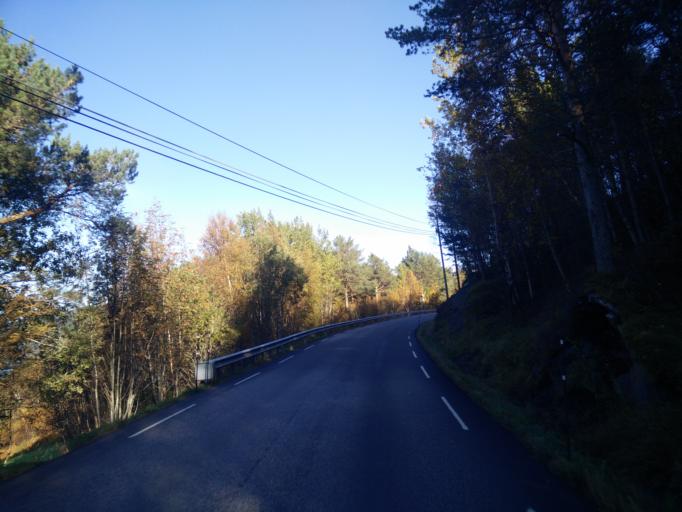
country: NO
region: More og Romsdal
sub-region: Halsa
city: Liaboen
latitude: 63.1370
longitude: 8.4125
